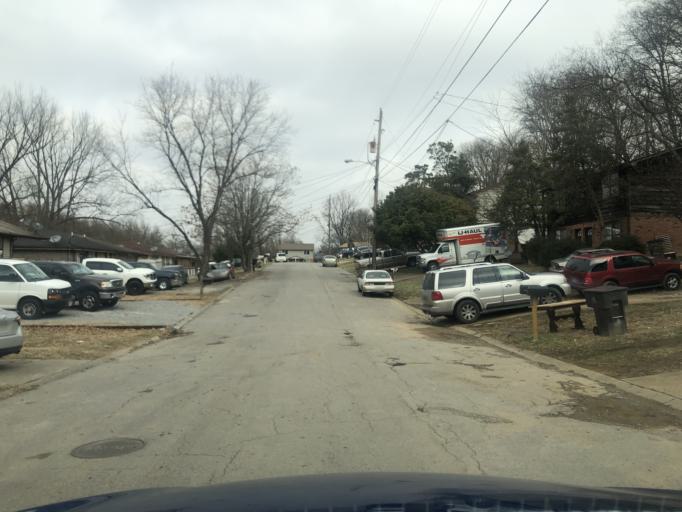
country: US
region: Tennessee
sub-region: Davidson County
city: Oak Hill
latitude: 36.0928
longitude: -86.7127
